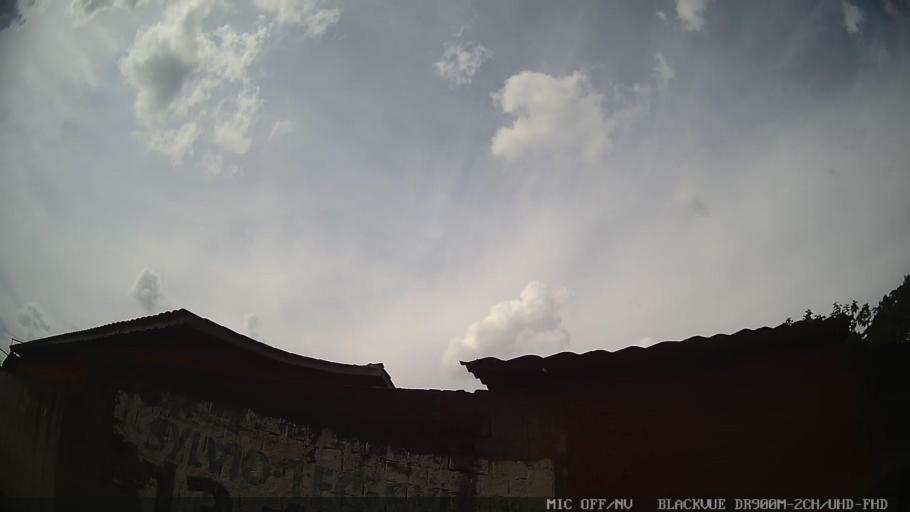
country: BR
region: Sao Paulo
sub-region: Braganca Paulista
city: Braganca Paulista
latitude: -22.9385
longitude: -46.5164
